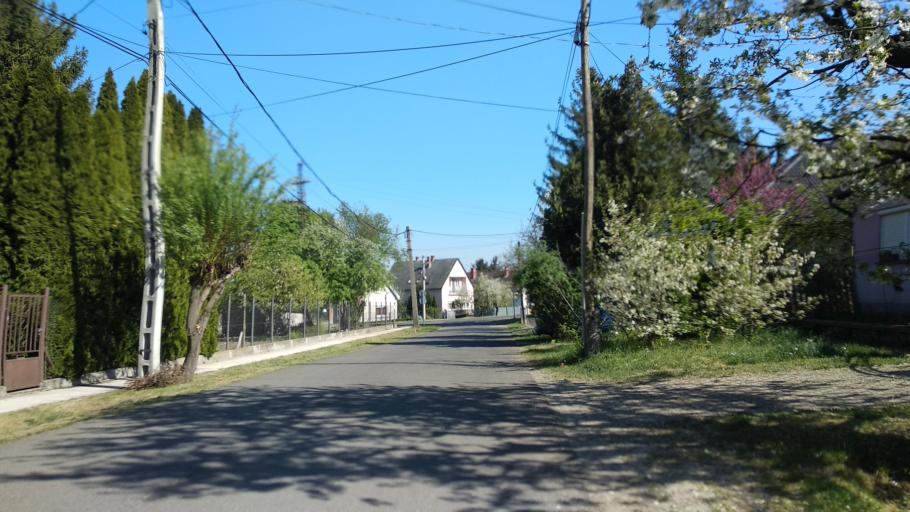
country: HU
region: Pest
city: Godollo
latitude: 47.5884
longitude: 19.3520
